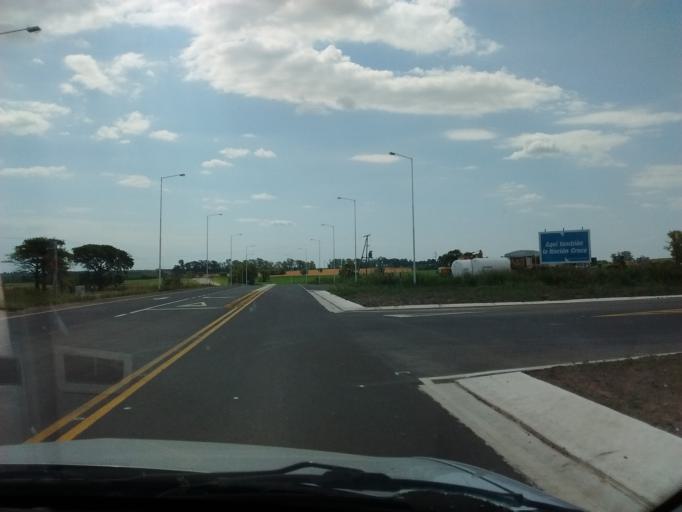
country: AR
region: Entre Rios
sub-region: Departamento de Victoria
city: Victoria
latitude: -32.6602
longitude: -60.0538
